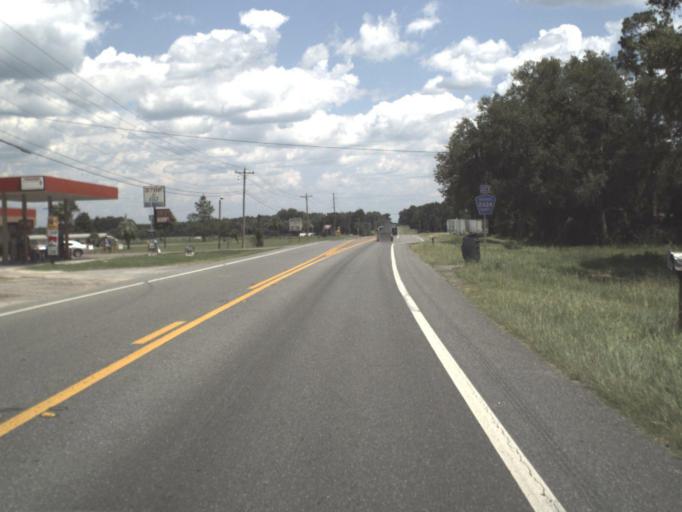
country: US
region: Florida
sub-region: Columbia County
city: Lake City
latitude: 30.1218
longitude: -82.6196
